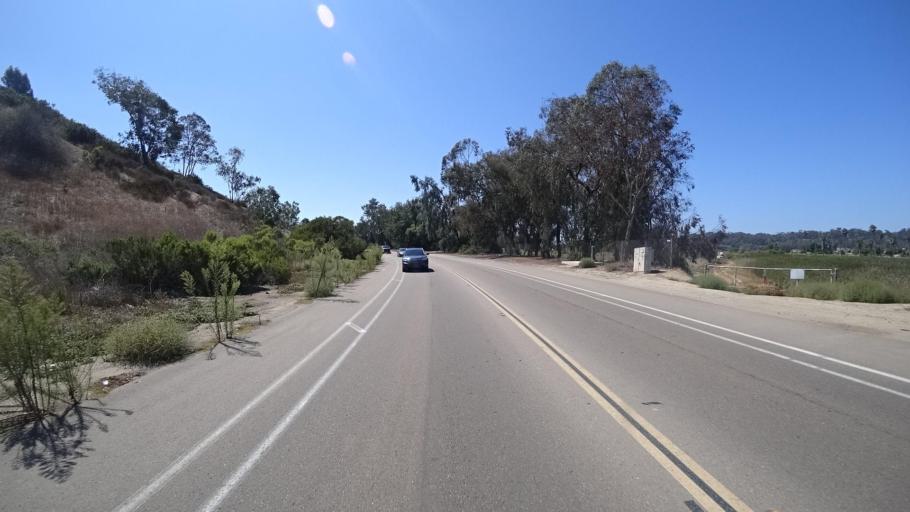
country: US
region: California
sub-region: San Diego County
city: Fairbanks Ranch
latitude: 32.9841
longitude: -117.2042
